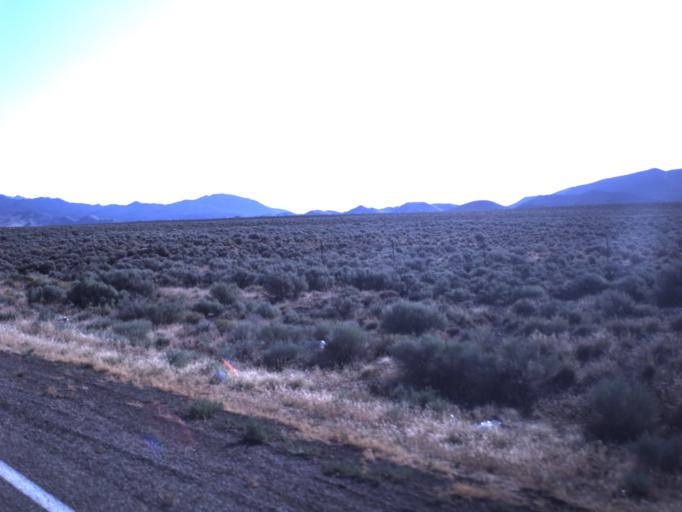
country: US
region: Utah
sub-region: Beaver County
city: Milford
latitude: 38.1638
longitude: -112.9552
